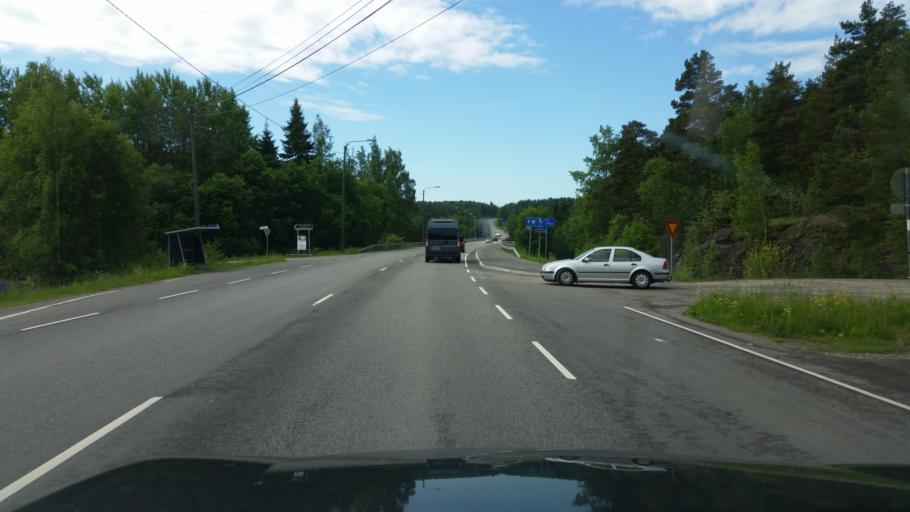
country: FI
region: Varsinais-Suomi
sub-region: Aboland-Turunmaa
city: Pargas
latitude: 60.3255
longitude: 22.3463
